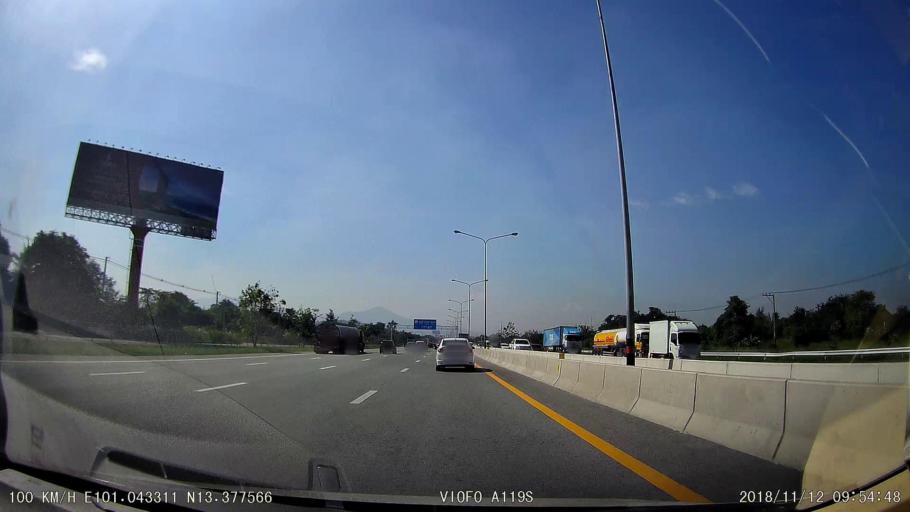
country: TH
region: Chon Buri
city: Chon Buri
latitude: 13.3766
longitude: 101.0427
